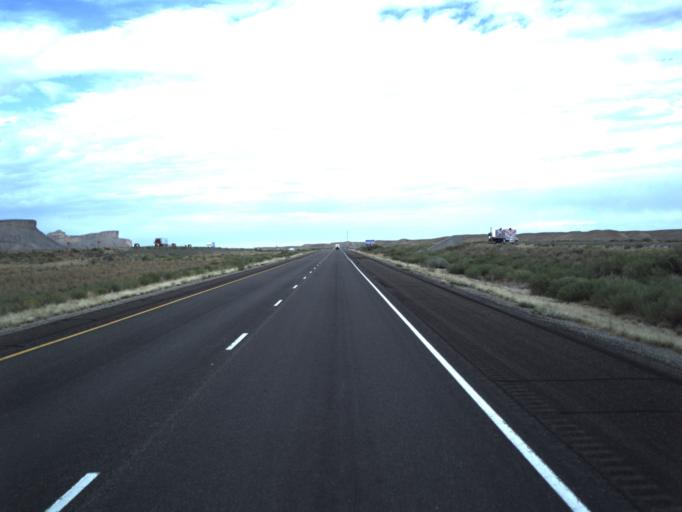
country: US
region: Utah
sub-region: Grand County
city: Moab
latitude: 38.9543
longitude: -109.7556
